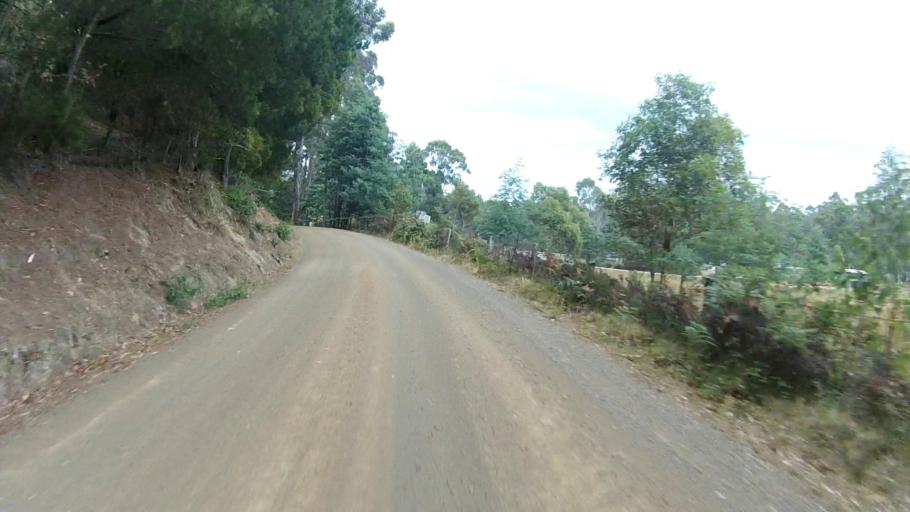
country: AU
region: Tasmania
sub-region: Huon Valley
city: Cygnet
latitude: -43.2313
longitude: 147.1591
